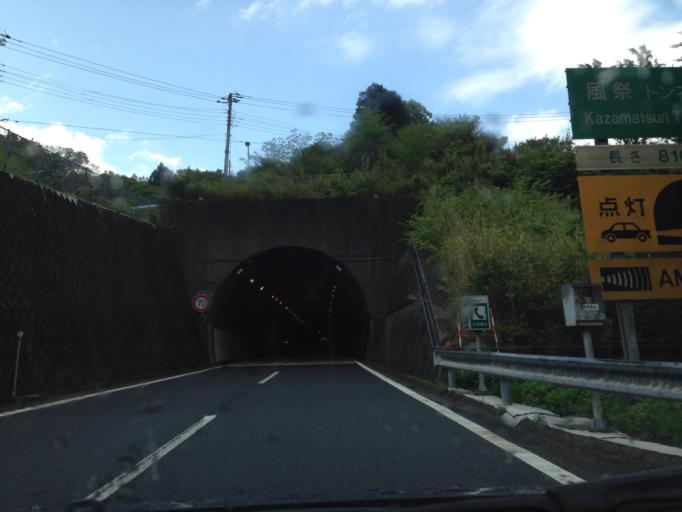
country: JP
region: Kanagawa
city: Odawara
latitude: 35.2486
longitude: 139.1329
